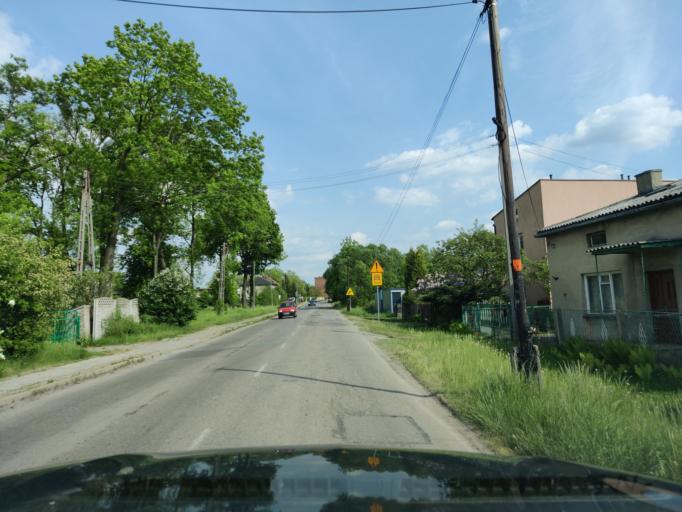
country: PL
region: Silesian Voivodeship
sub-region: Powiat bedzinski
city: Siewierz
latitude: 50.3974
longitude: 19.2380
